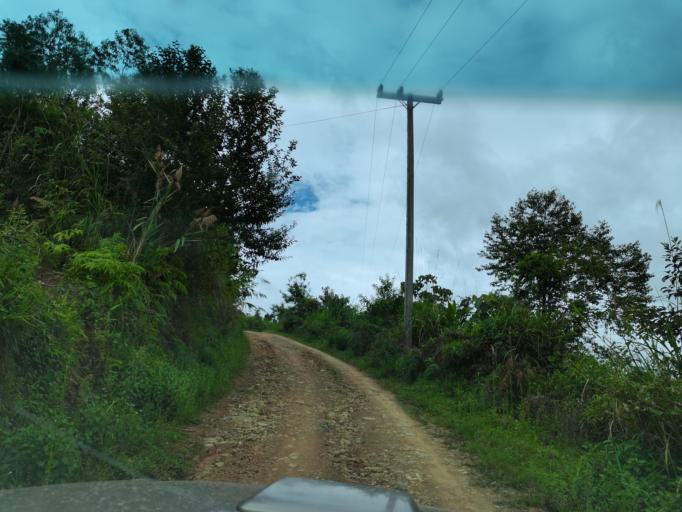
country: LA
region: Phongsali
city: Phongsali
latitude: 21.6647
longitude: 102.1796
